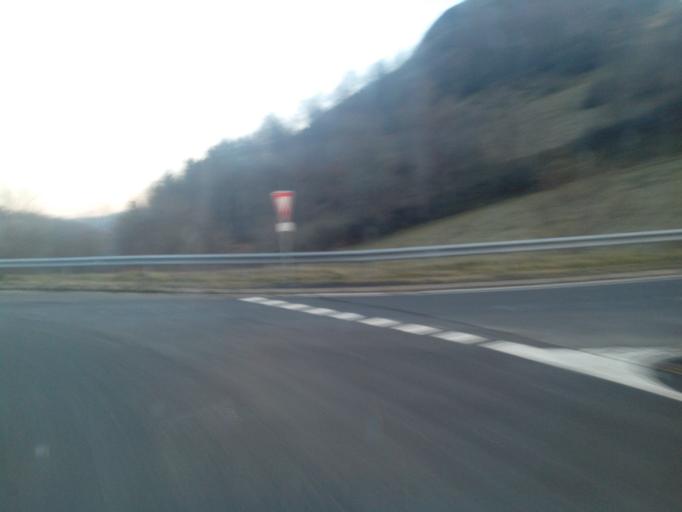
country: FR
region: Auvergne
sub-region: Departement du Cantal
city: Murat
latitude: 45.1142
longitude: 2.8631
